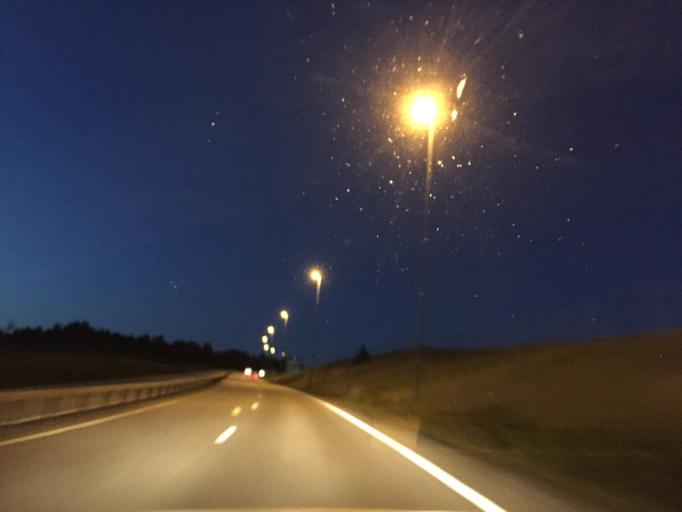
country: NO
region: Akershus
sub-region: Nes
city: Neskollen
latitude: 60.1177
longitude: 11.2837
